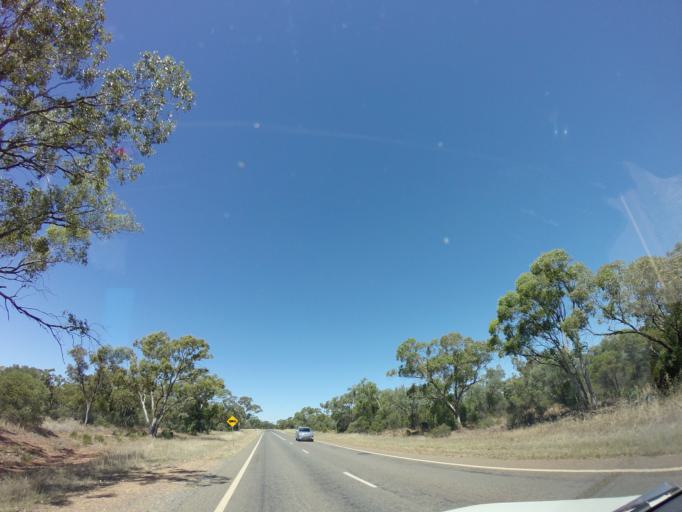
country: AU
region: New South Wales
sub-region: Bogan
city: Nyngan
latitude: -31.5460
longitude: 146.7311
